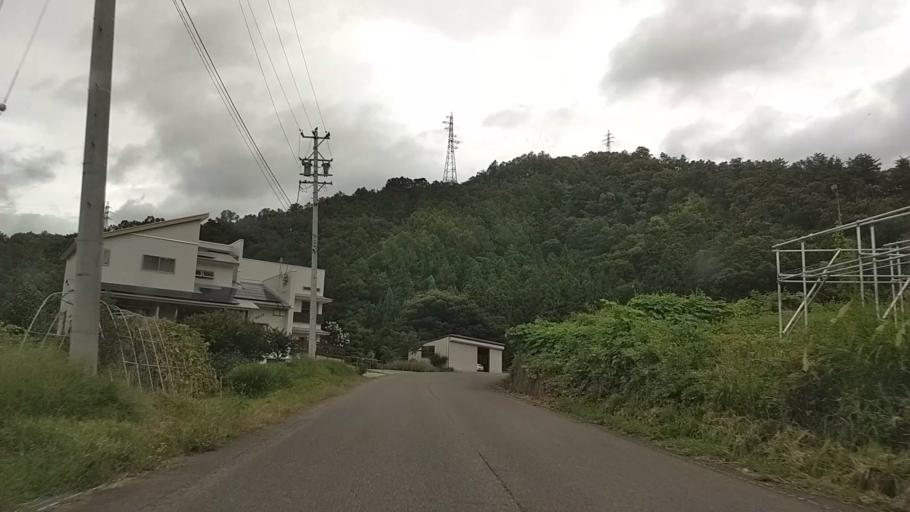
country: JP
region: Nagano
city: Iiyama
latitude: 36.8171
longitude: 138.3667
